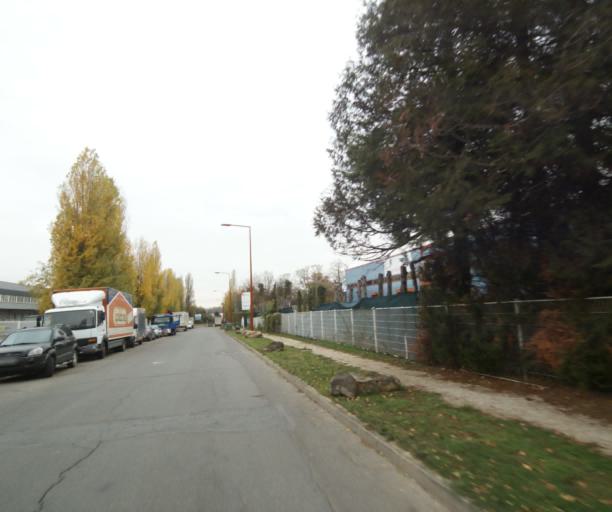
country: FR
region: Ile-de-France
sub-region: Departement du Val-d'Oise
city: Gonesse
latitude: 48.9834
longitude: 2.4612
